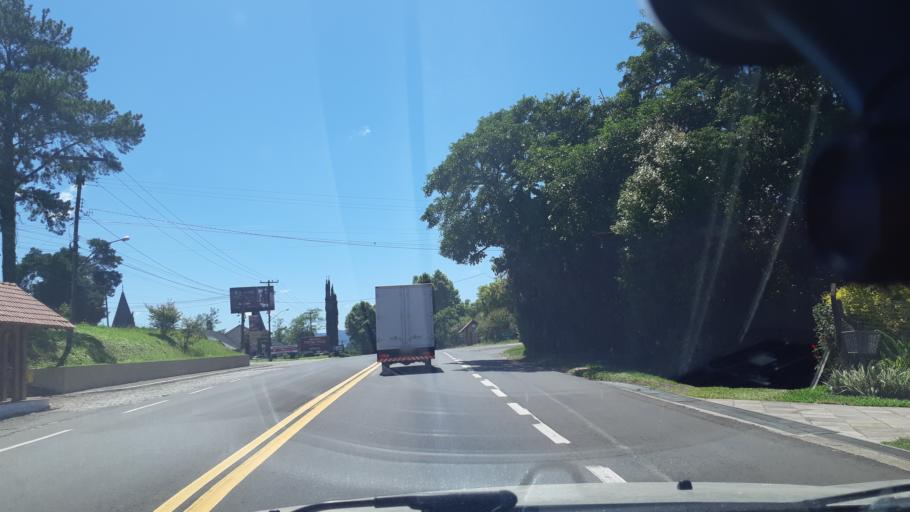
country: BR
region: Rio Grande do Sul
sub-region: Ivoti
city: Ivoti
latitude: -29.6216
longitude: -51.1284
